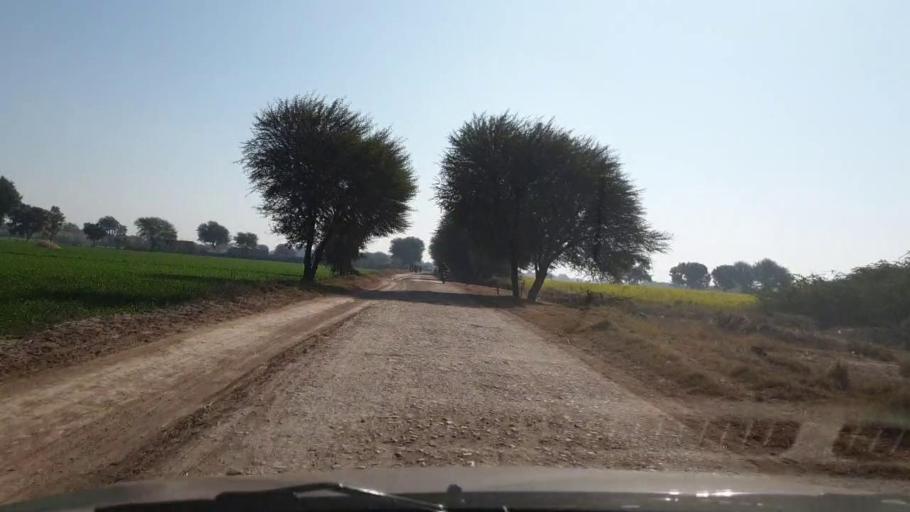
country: PK
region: Sindh
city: Jhol
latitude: 25.9355
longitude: 68.8224
